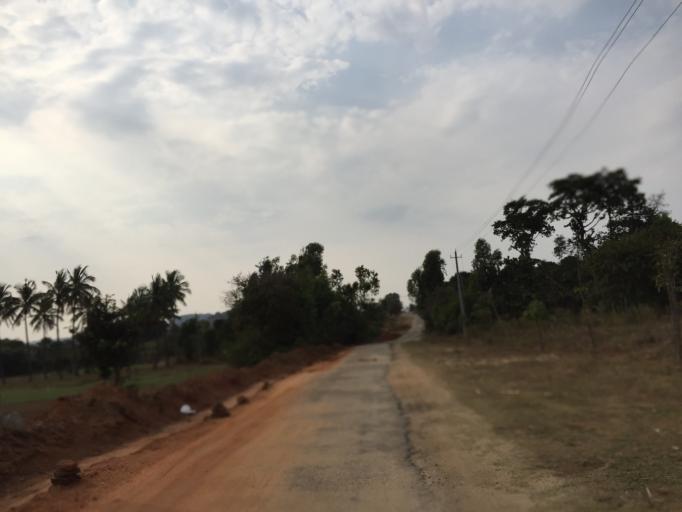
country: IN
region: Karnataka
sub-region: Chikkaballapur
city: Gudibanda
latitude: 13.5763
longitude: 77.7246
